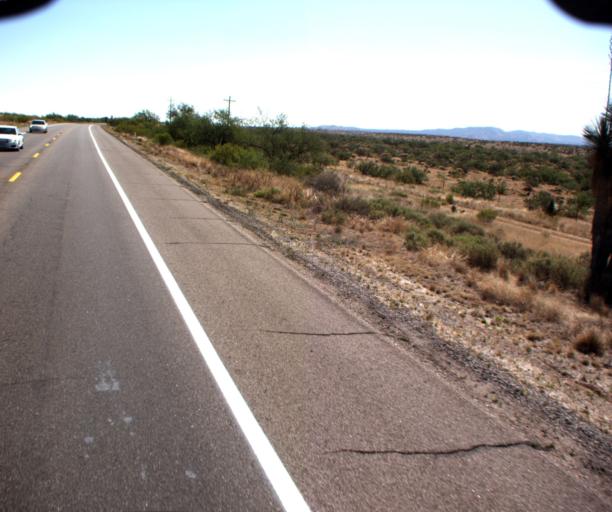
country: US
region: Arizona
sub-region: Pima County
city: Catalina
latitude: 32.5845
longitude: -110.9054
